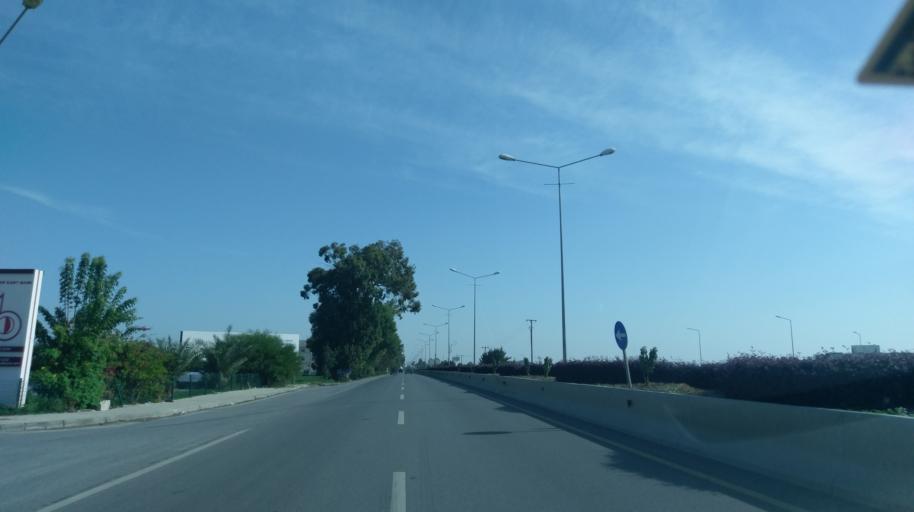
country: CY
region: Lefkosia
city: Nicosia
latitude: 35.2195
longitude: 33.4687
